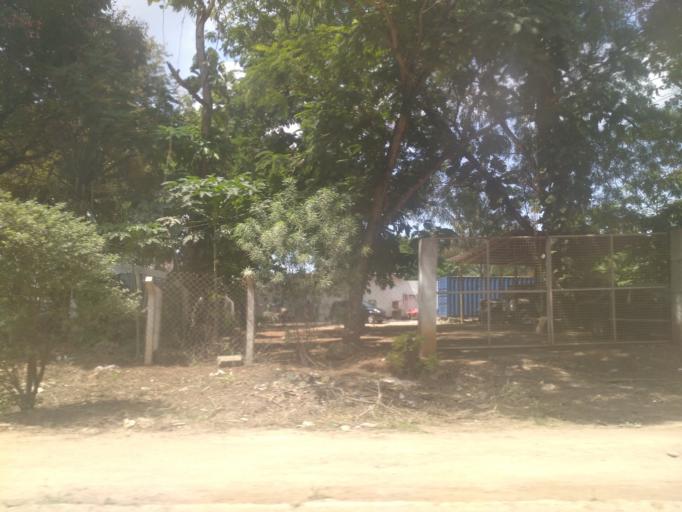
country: TZ
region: Zanzibar Urban/West
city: Zanzibar
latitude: -6.2166
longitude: 39.2203
